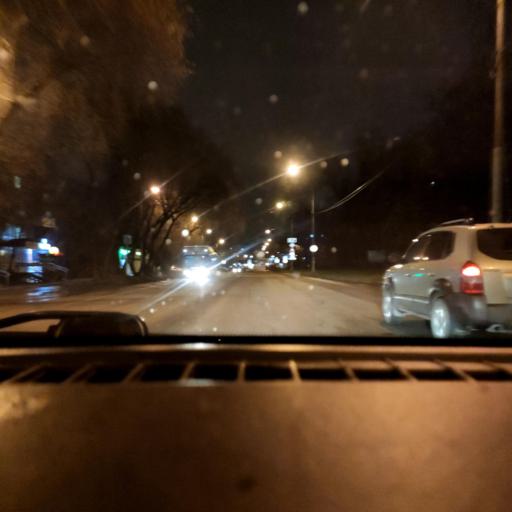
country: RU
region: Perm
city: Perm
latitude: 57.9734
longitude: 56.2378
